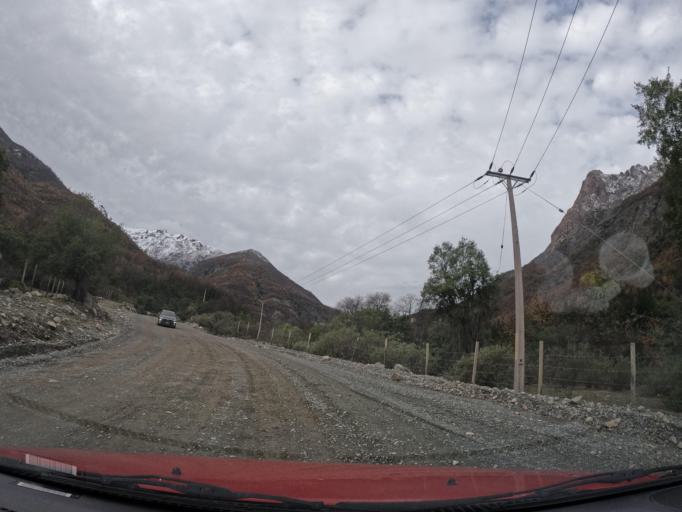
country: CL
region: Maule
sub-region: Provincia de Linares
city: Colbun
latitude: -35.8570
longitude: -71.2005
